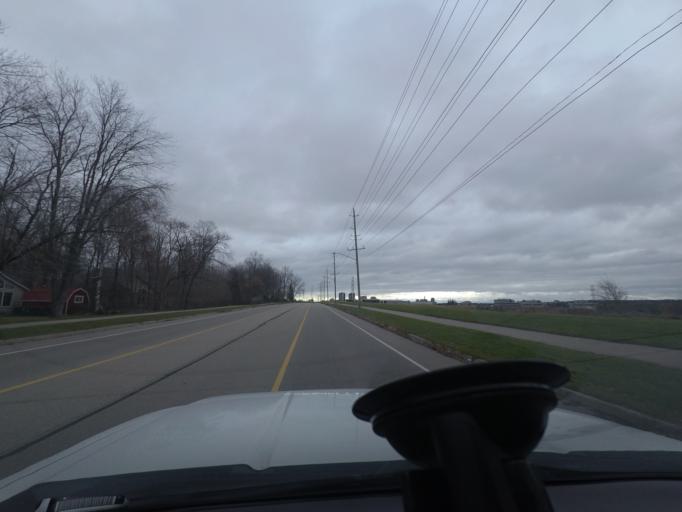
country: CN
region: Xinjiang Uygur Zizhiqu
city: Ayxin Siri
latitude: 43.4837
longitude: 80.5589
